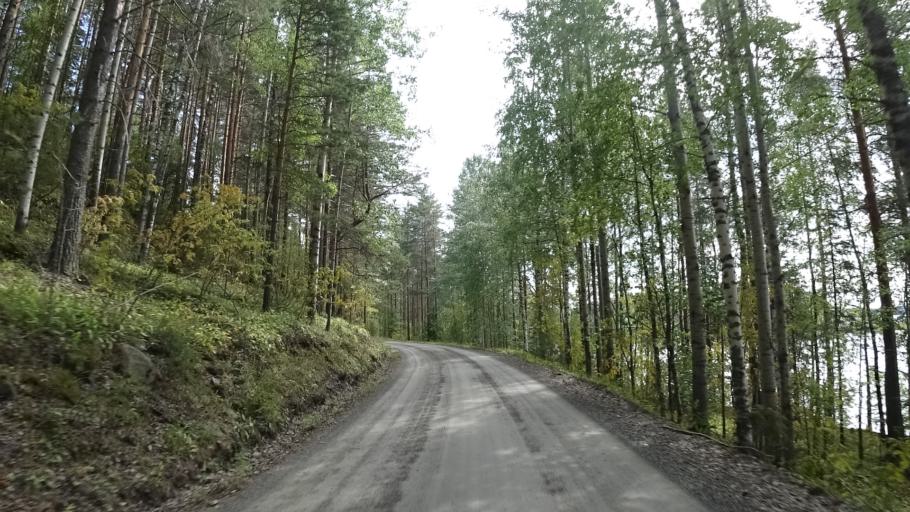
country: FI
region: North Karelia
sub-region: Joensuu
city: Pyhaeselkae
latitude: 62.3766
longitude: 29.8113
